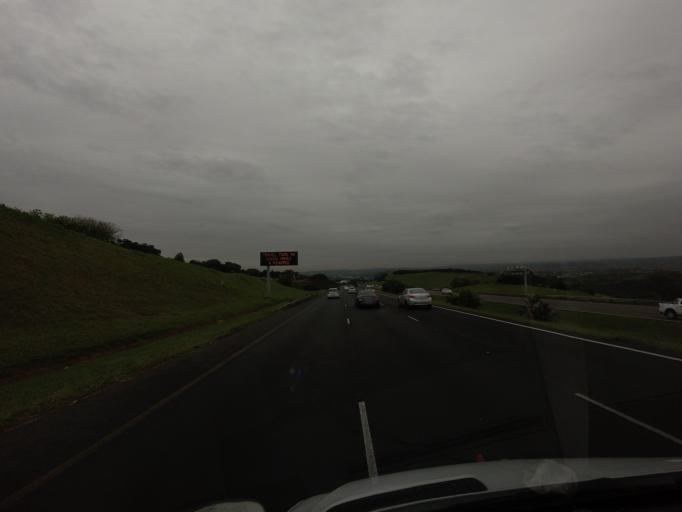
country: ZA
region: KwaZulu-Natal
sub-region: eThekwini Metropolitan Municipality
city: Durban
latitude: -29.7429
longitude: 31.0425
